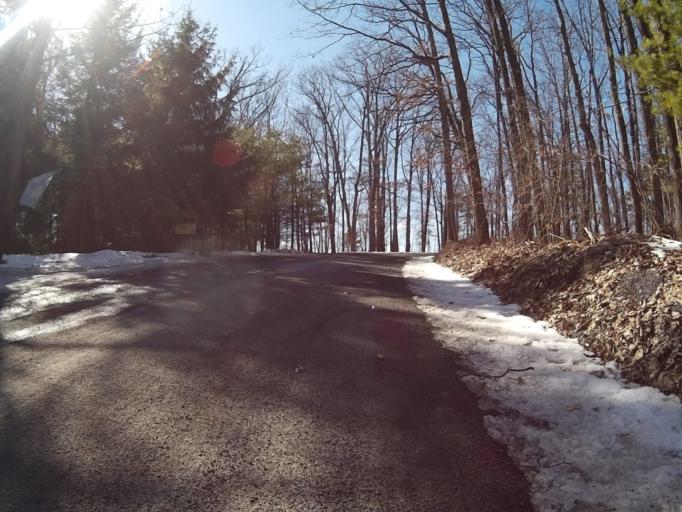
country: US
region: Pennsylvania
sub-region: Centre County
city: Stormstown
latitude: 40.8462
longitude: -78.0396
